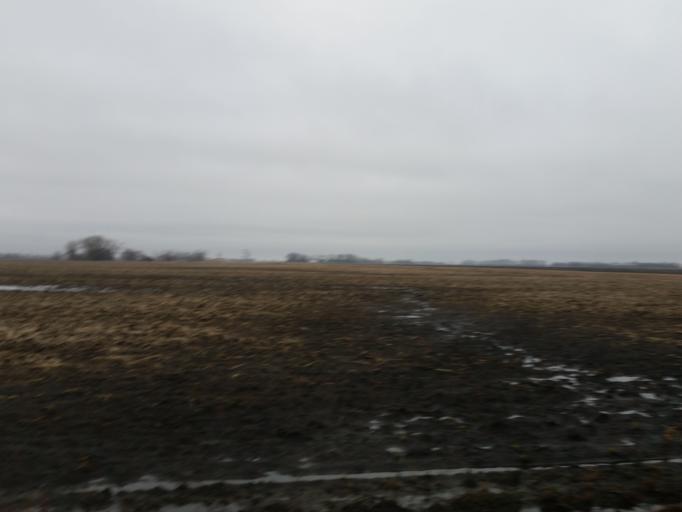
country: US
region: North Dakota
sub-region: Walsh County
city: Grafton
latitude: 48.3822
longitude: -97.1683
